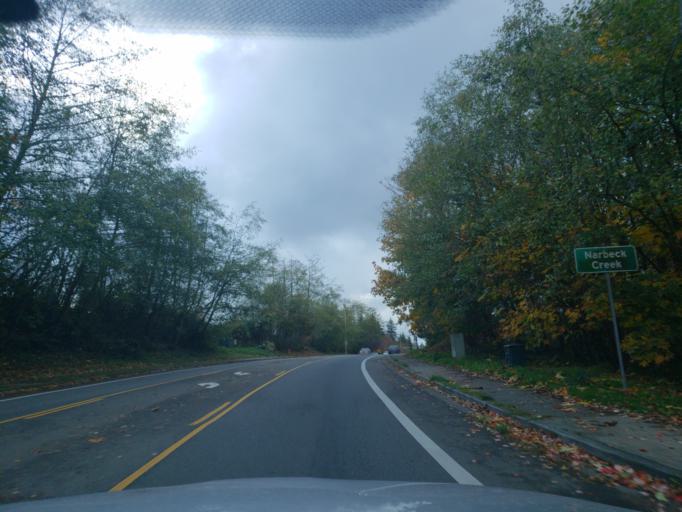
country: US
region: Washington
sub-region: Snohomish County
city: Mukilteo
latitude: 47.9413
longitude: -122.2606
